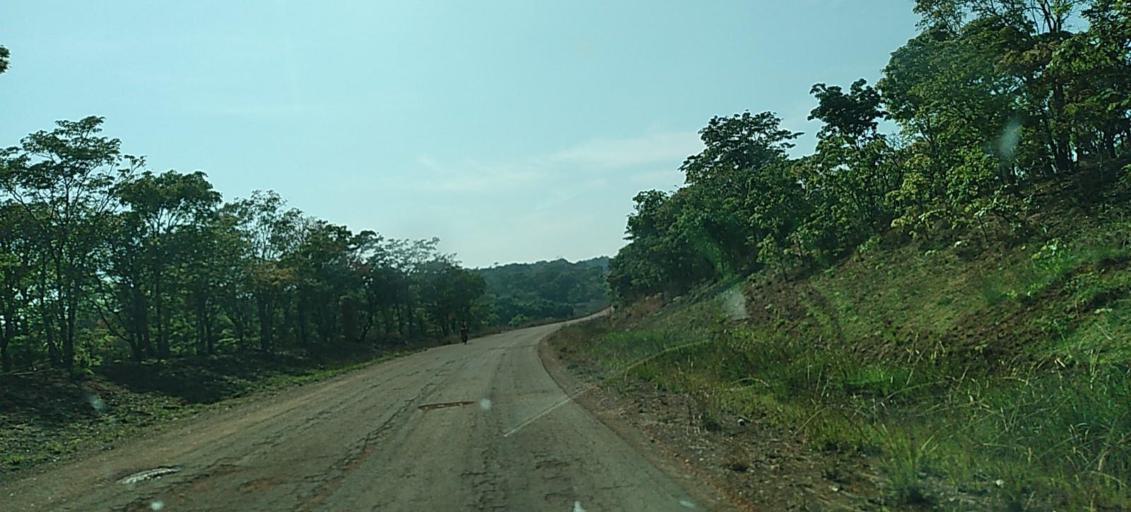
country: ZM
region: North-Western
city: Mwinilunga
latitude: -11.7849
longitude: 25.0436
